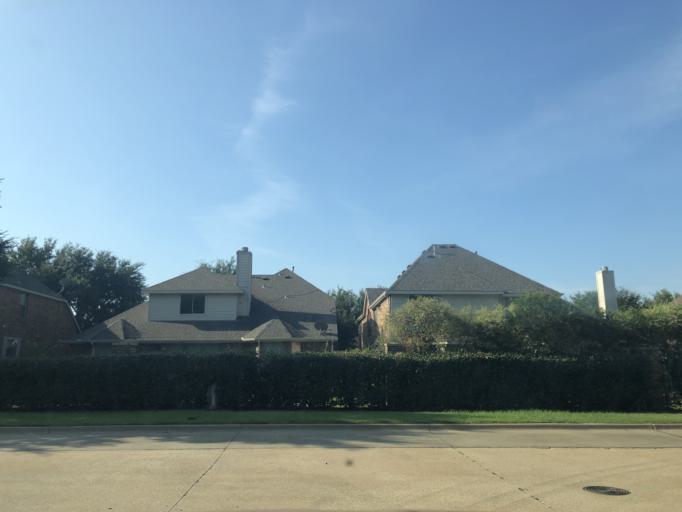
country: US
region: Texas
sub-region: Tarrant County
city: Euless
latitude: 32.8740
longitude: -97.0926
